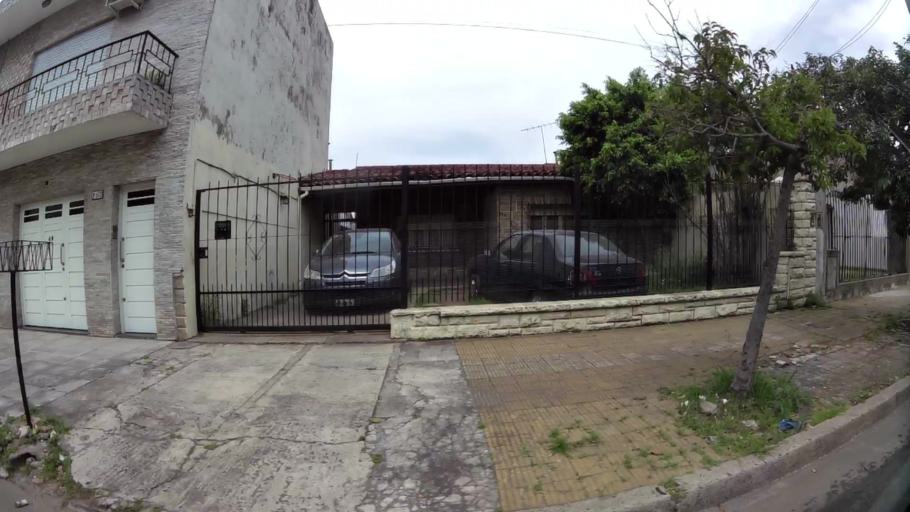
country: AR
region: Buenos Aires
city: San Justo
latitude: -34.6685
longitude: -58.5413
